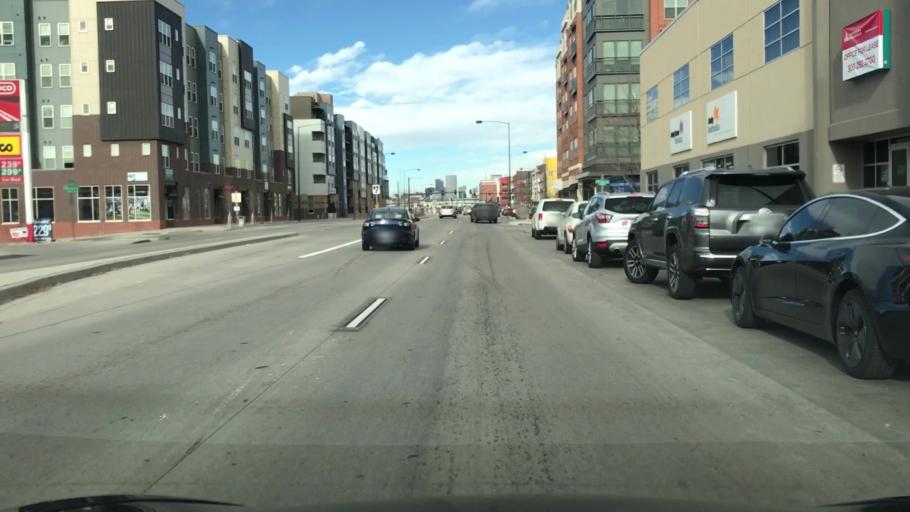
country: US
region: Colorado
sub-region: Denver County
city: Denver
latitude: 39.6943
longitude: -104.9874
